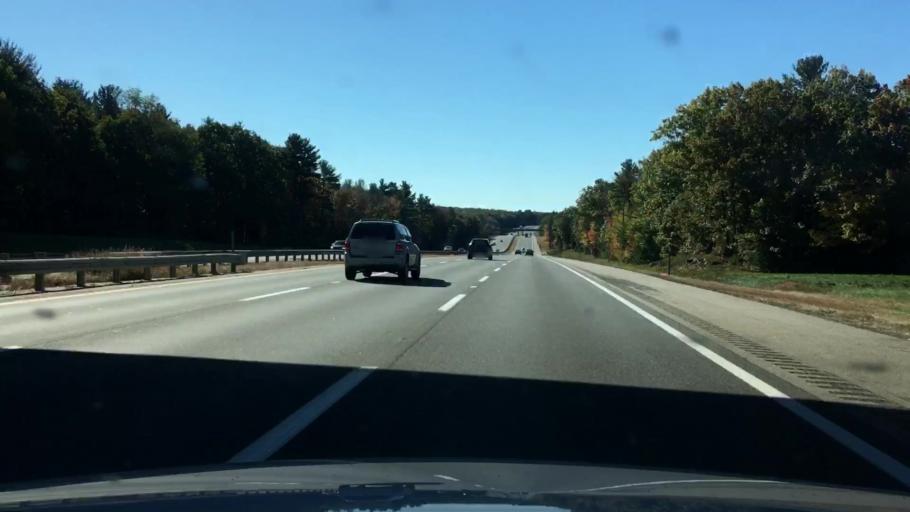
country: US
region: Maine
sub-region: York County
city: Ogunquit
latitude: 43.2716
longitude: -70.6186
